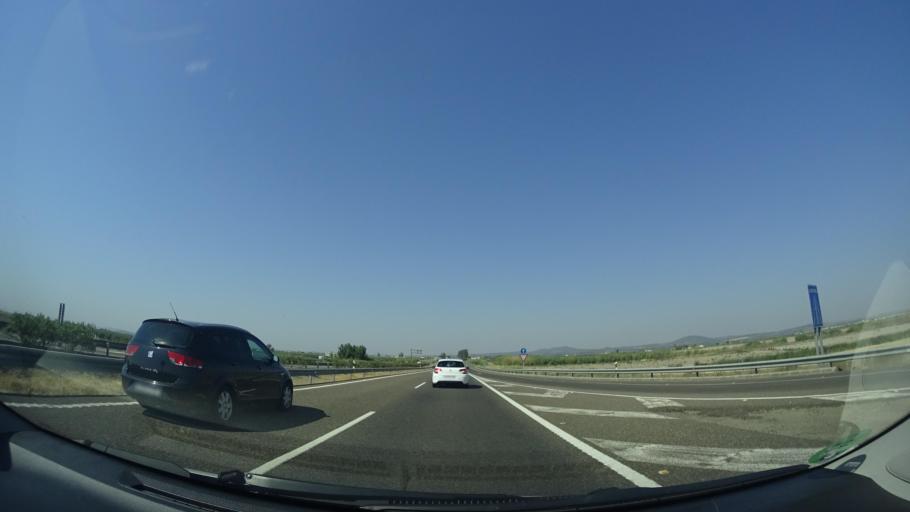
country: ES
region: Extremadura
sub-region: Provincia de Caceres
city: Miajadas
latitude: 39.1150
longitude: -5.9773
